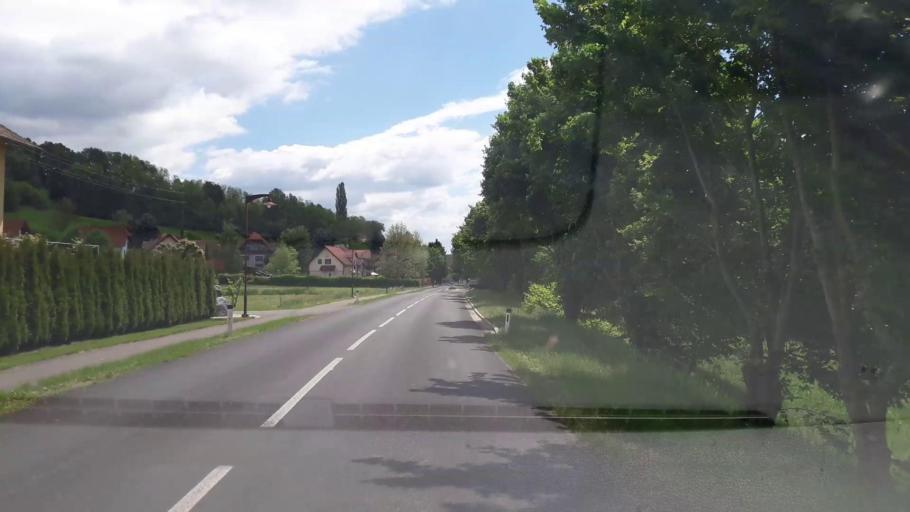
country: AT
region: Styria
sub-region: Politischer Bezirk Suedoststeiermark
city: Unterlamm
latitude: 46.9836
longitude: 16.0545
